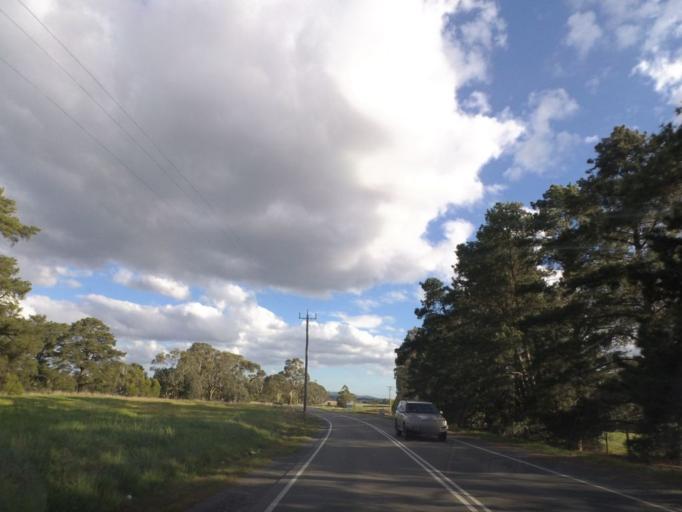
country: AU
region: Victoria
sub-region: Yarra Ranges
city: Yarra Glen
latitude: -37.6935
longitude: 145.3735
